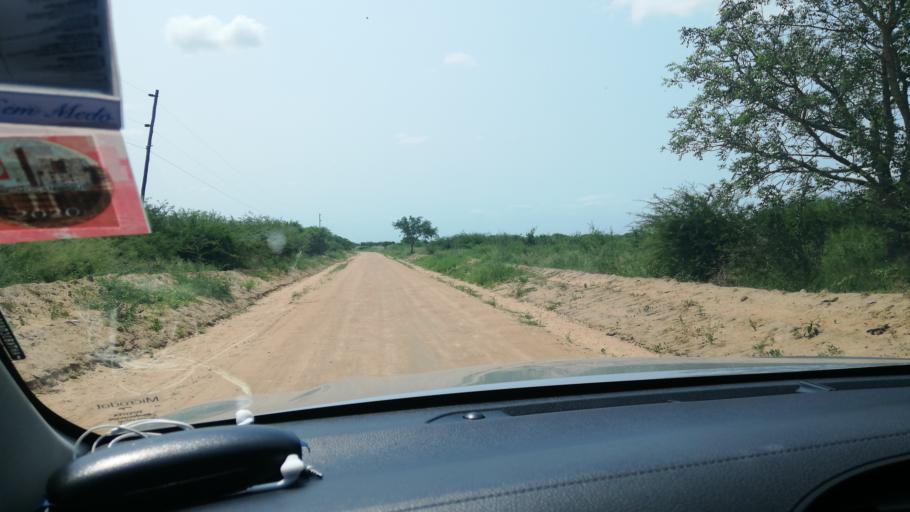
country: MZ
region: Maputo
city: Matola
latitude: -26.0895
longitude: 32.3909
